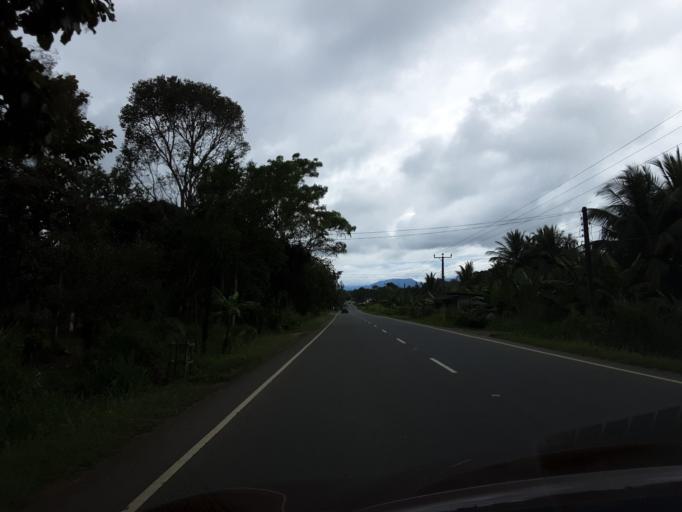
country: LK
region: Uva
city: Badulla
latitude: 7.3771
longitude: 81.0688
